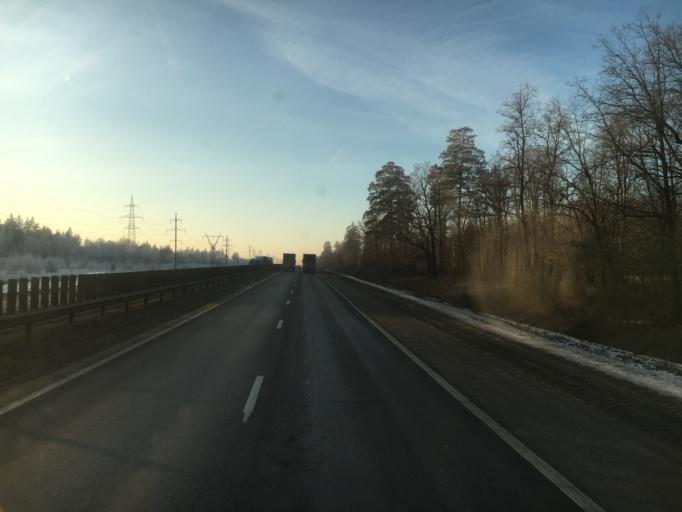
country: RU
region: Samara
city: Pribrezhnyy
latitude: 53.5159
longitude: 49.8675
